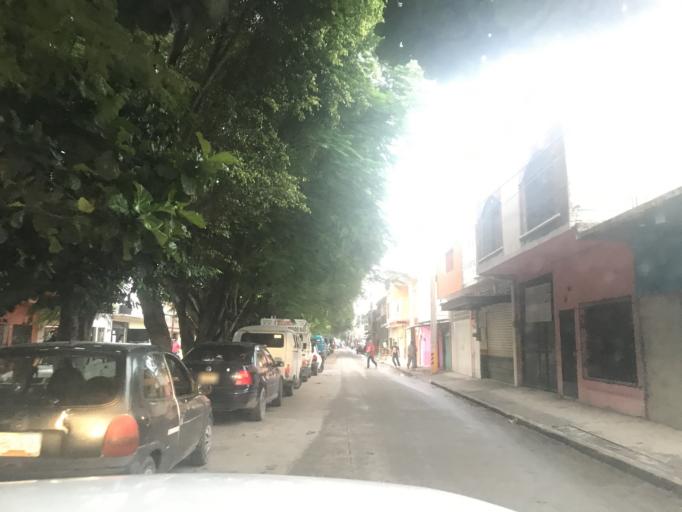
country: MX
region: Morelos
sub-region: Jojutla
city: Jojutla
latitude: 18.6137
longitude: -99.1760
